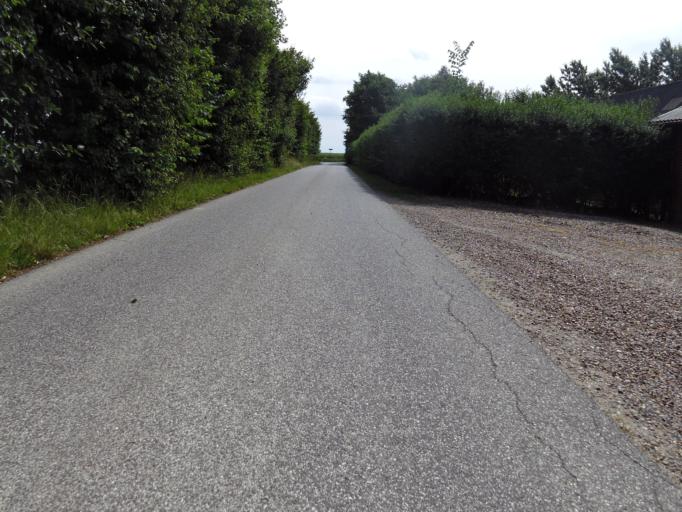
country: DK
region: Central Jutland
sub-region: Holstebro Kommune
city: Holstebro
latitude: 56.4282
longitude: 8.6662
